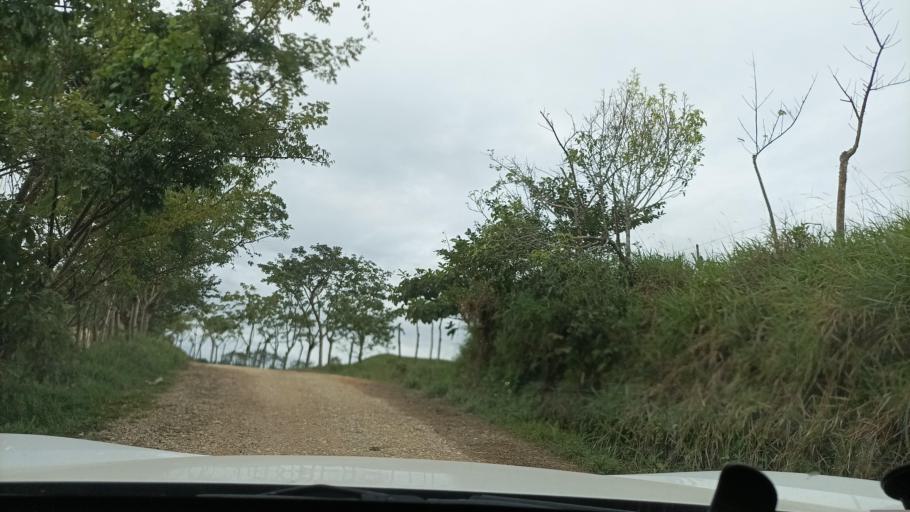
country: MX
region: Veracruz
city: Hidalgotitlan
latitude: 17.6007
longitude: -94.4229
